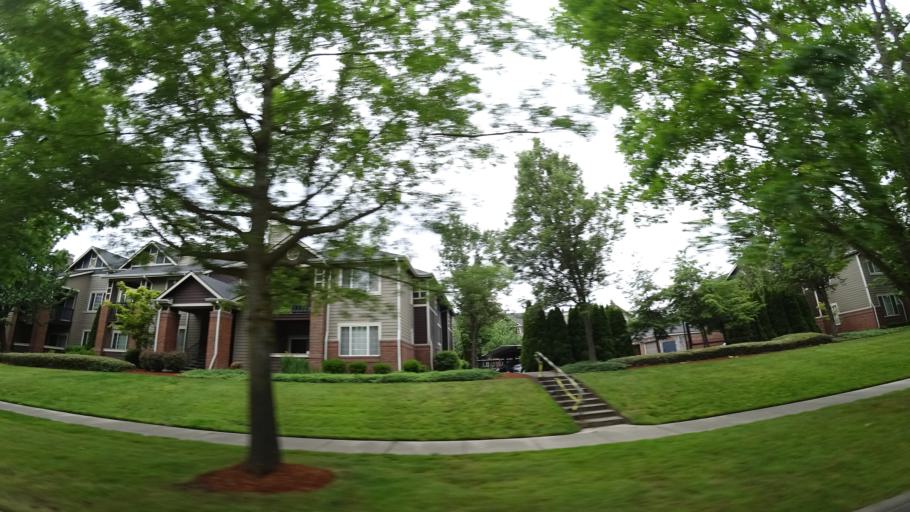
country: US
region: Oregon
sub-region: Washington County
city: Rockcreek
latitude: 45.5363
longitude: -122.9067
